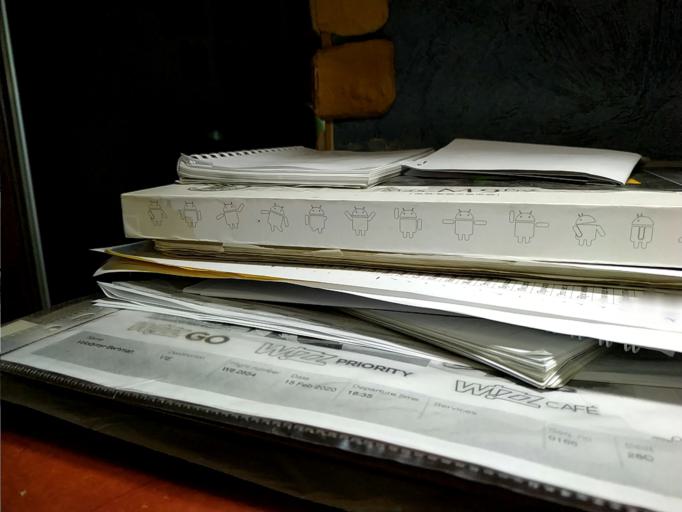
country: RU
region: Arkhangelskaya
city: Onega
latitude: 63.7608
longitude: 37.9921
